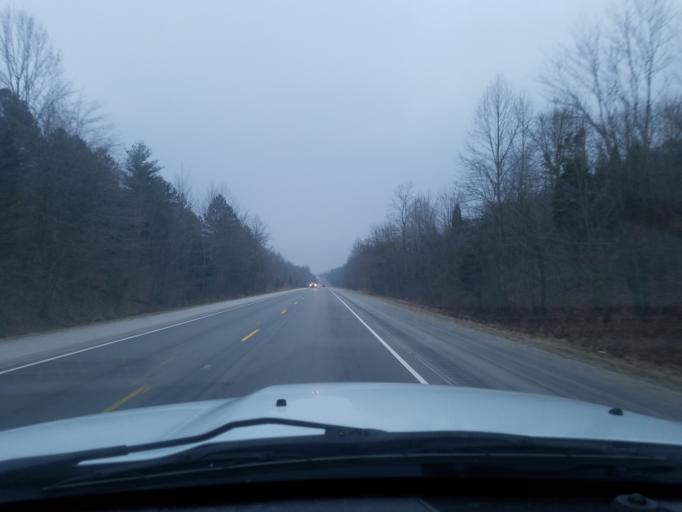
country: US
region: Indiana
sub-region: Crawford County
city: English
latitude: 38.1888
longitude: -86.6009
